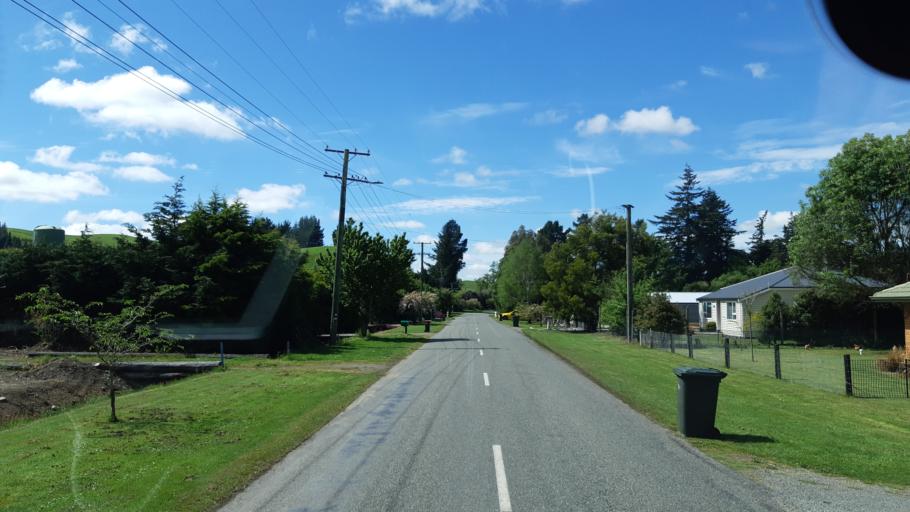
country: NZ
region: Canterbury
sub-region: Selwyn District
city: Darfield
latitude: -43.4716
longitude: 171.9050
